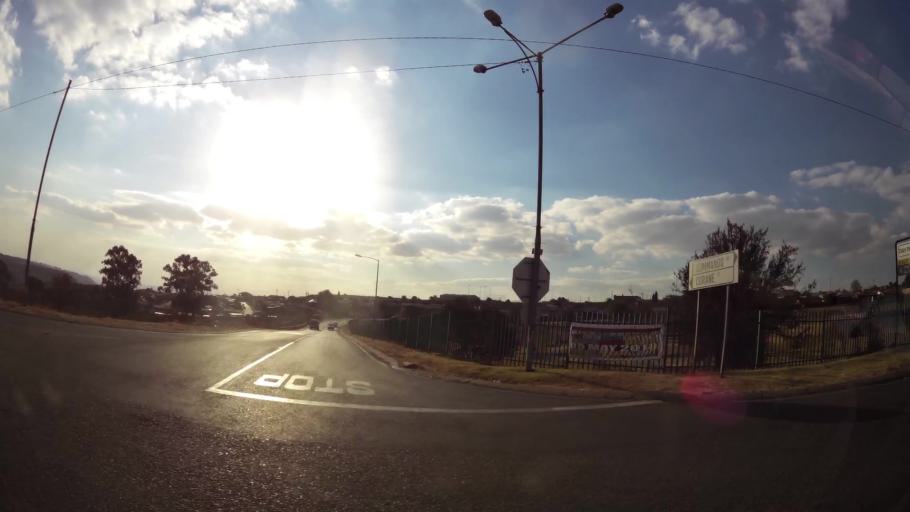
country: ZA
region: Gauteng
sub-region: West Rand District Municipality
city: Krugersdorp
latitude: -26.0835
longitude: 27.7542
